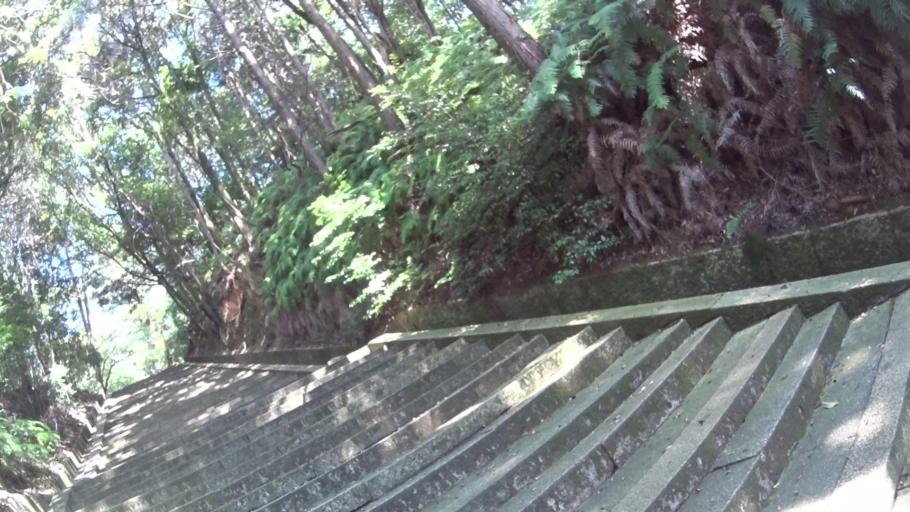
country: RU
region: Rostov
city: Remontnoye
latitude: 46.5000
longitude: 43.7692
